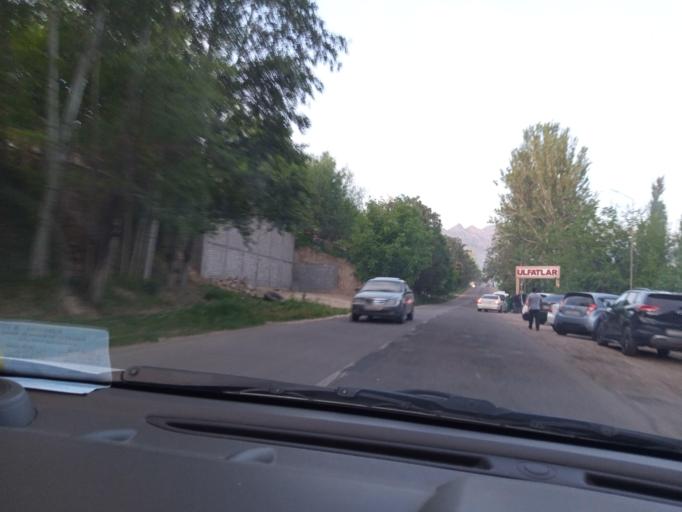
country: UZ
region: Toshkent
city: Parkent
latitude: 41.2472
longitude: 69.7593
